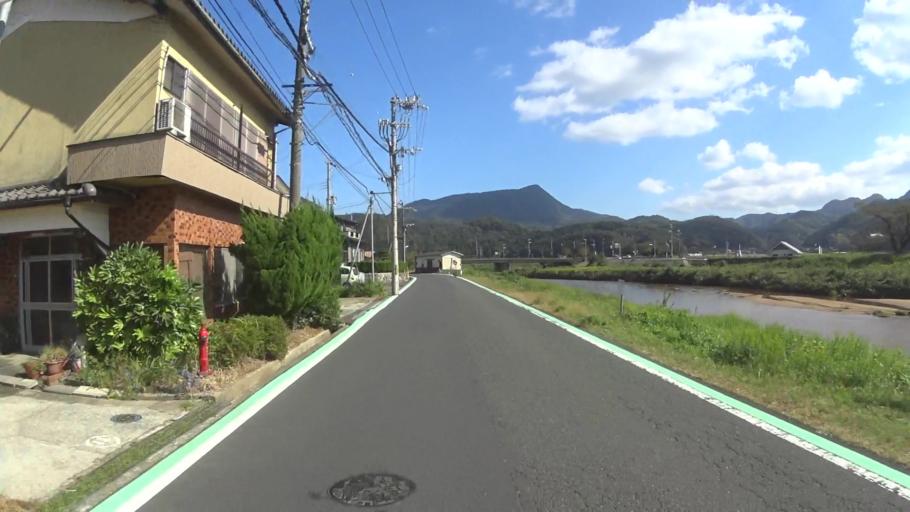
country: JP
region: Kyoto
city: Miyazu
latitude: 35.7125
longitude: 135.1037
